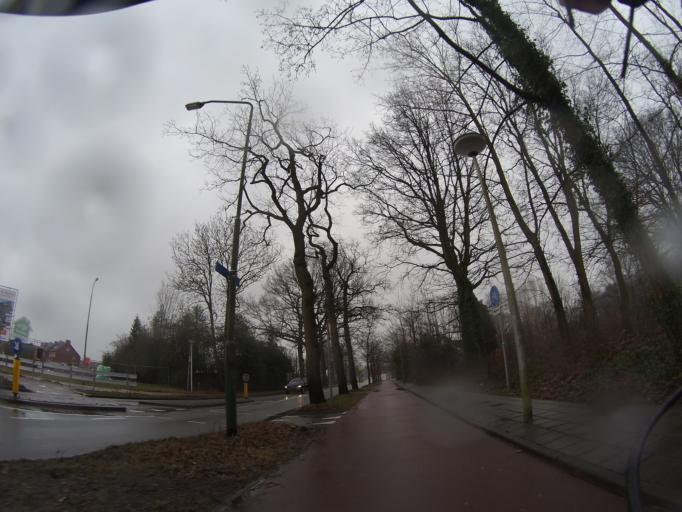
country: NL
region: Utrecht
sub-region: Gemeente Amersfoort
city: Randenbroek
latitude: 52.1456
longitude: 5.4041
